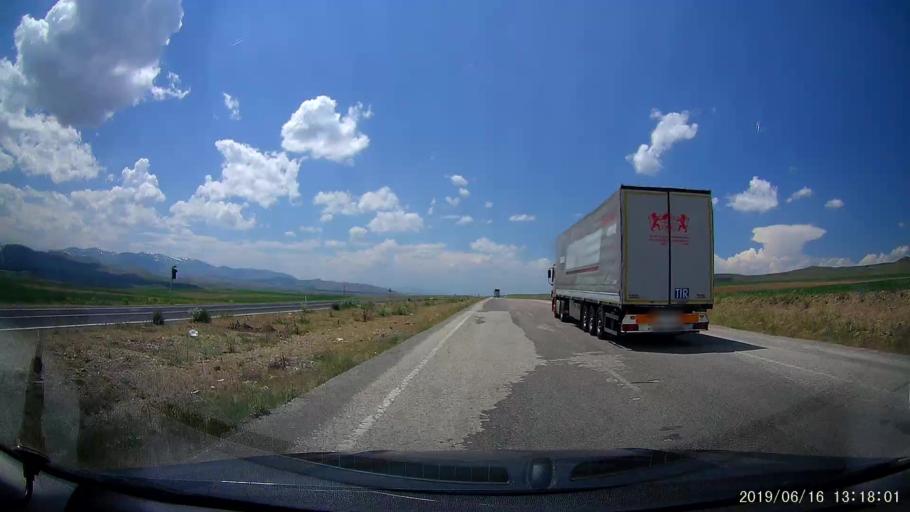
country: TR
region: Agri
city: Taslicay
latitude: 39.6290
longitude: 43.4400
